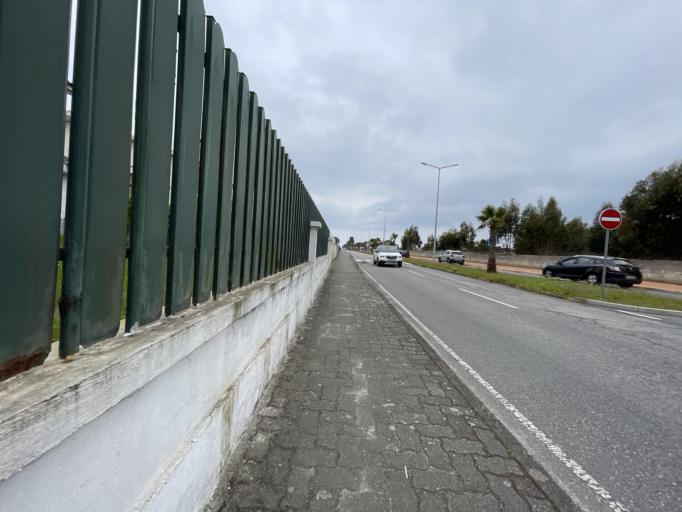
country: PT
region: Aveiro
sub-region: Ovar
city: Ovar
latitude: 40.8668
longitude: -8.6606
